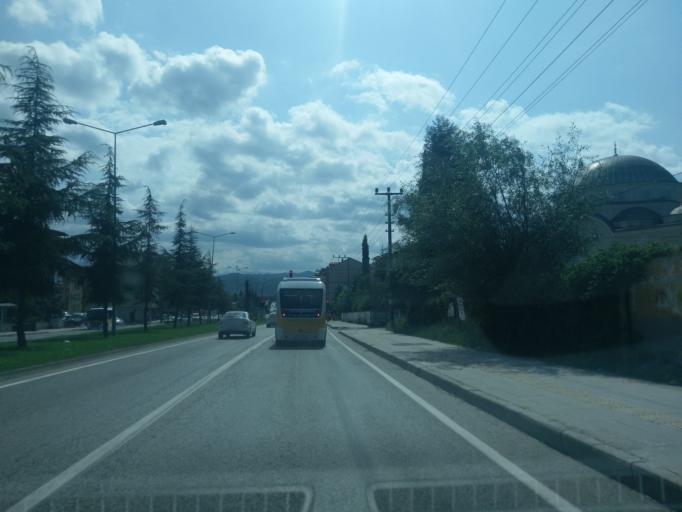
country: TR
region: Ordu
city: Ordu
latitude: 40.9582
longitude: 37.8968
